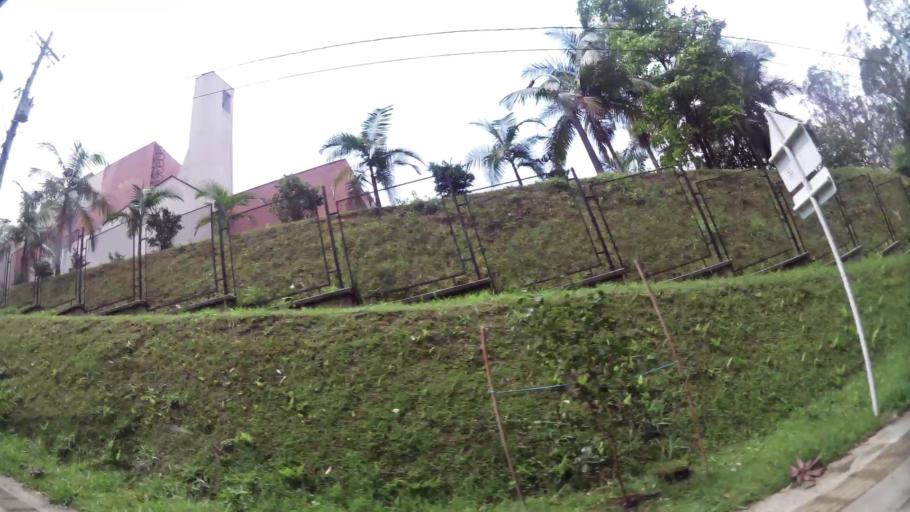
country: CO
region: Antioquia
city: Medellin
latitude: 6.2046
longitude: -75.5471
